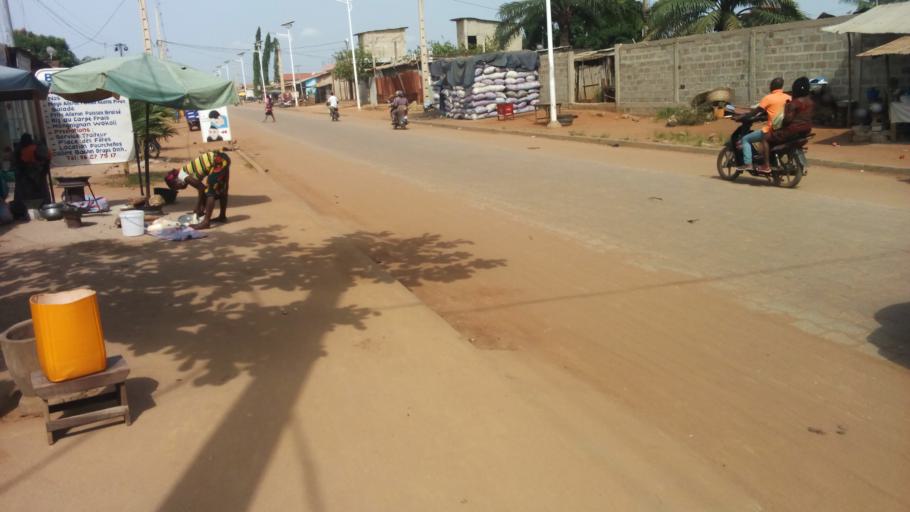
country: BJ
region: Atlantique
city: Abomey-Calavi
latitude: 6.4253
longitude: 2.3222
